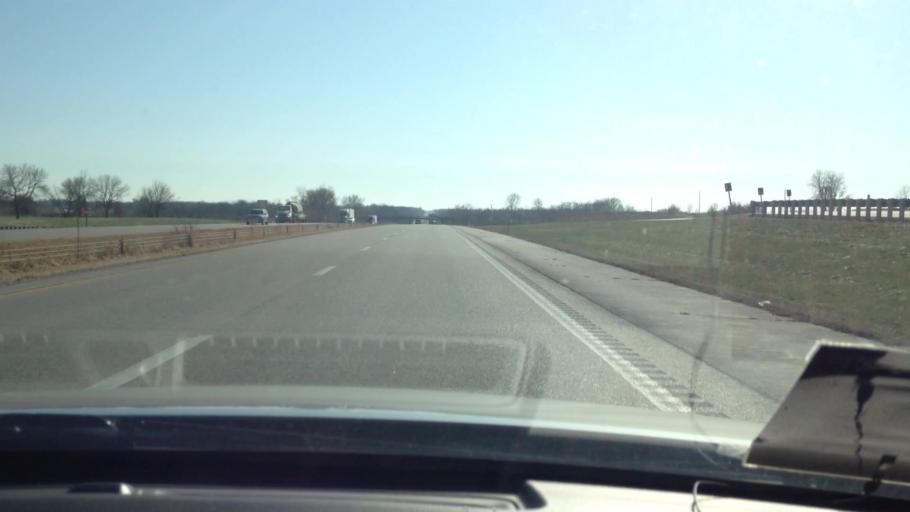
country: US
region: Missouri
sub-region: Platte County
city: Platte City
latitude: 39.4760
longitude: -94.7874
